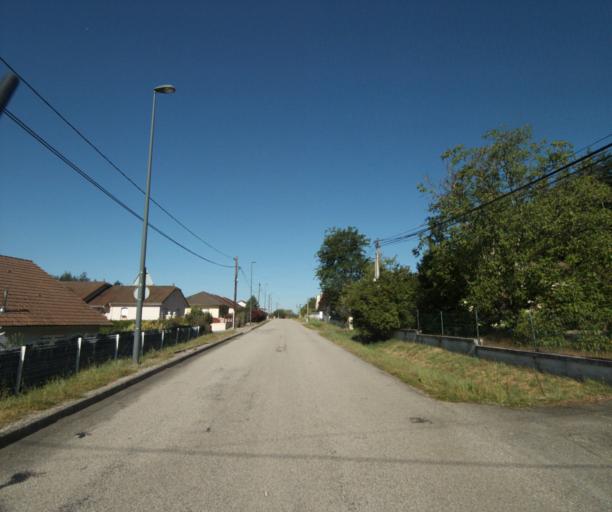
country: FR
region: Lorraine
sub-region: Departement des Vosges
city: Deyvillers
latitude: 48.1701
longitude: 6.5258
